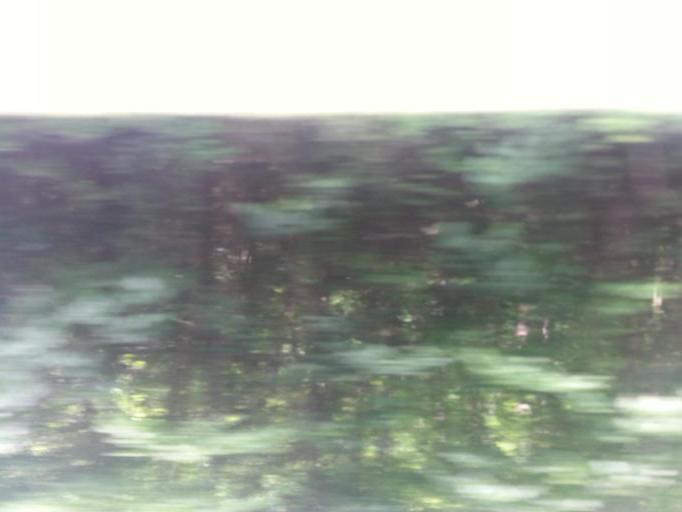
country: US
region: Georgia
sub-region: Towns County
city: Hiawassee
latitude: 34.8553
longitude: -83.7896
